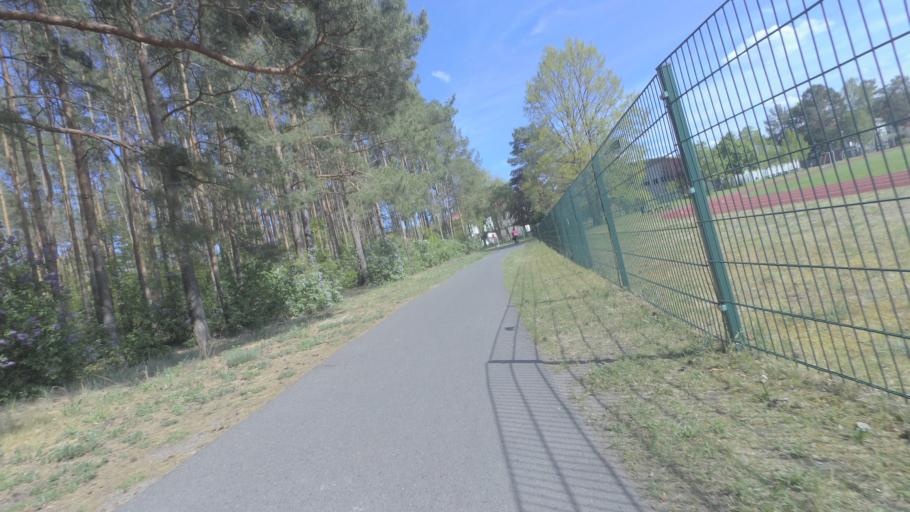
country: DE
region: Brandenburg
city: Grunheide
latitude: 52.4157
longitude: 13.8220
